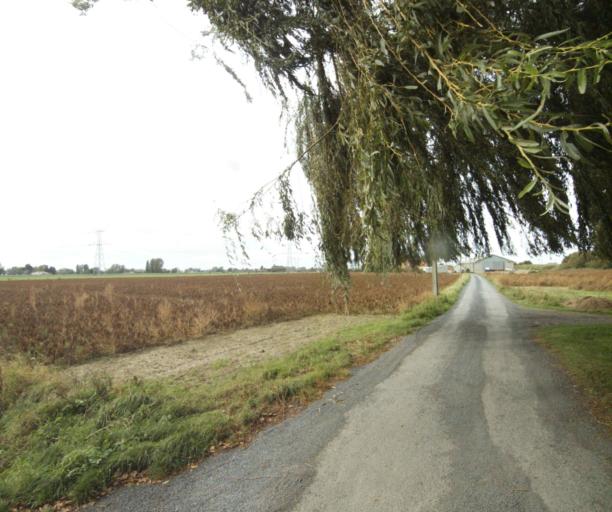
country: FR
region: Nord-Pas-de-Calais
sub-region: Departement du Nord
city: Radinghem-en-Weppes
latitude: 50.6428
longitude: 2.9066
